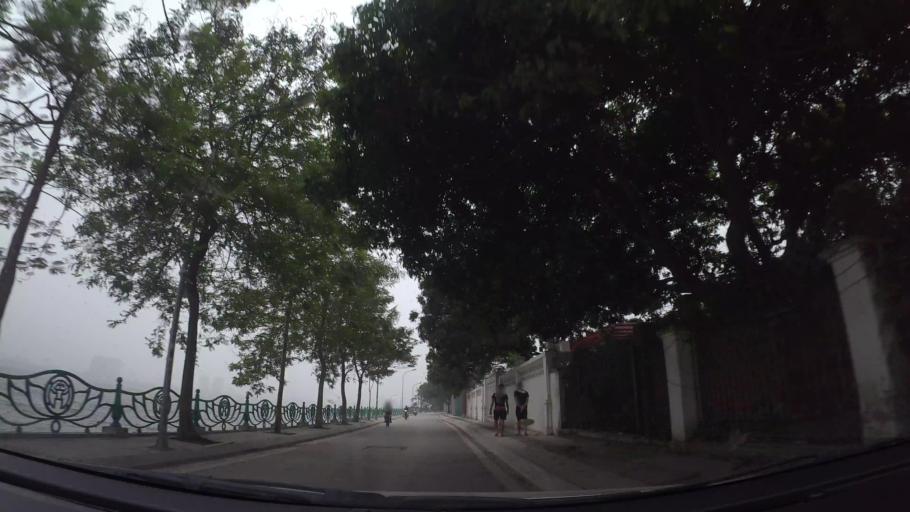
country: VN
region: Ha Noi
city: Tay Ho
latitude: 21.0596
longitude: 105.8265
